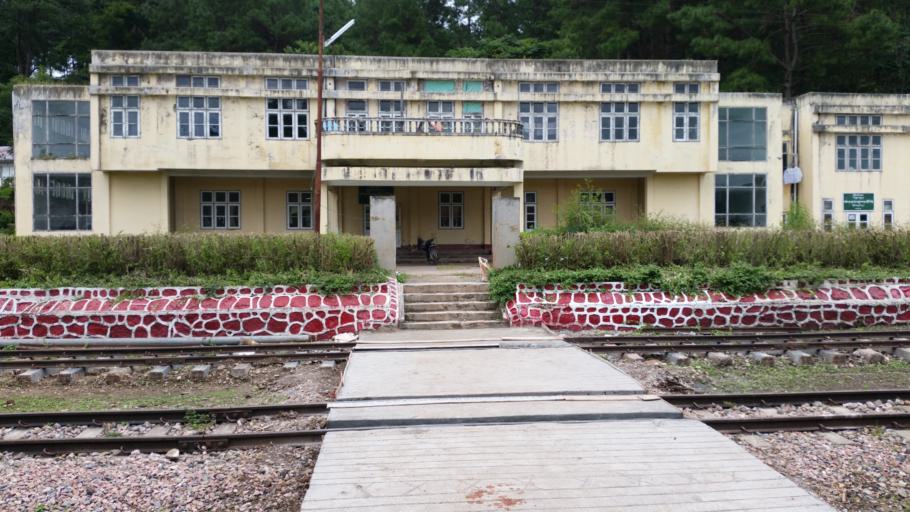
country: MM
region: Mandalay
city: Yamethin
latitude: 20.6290
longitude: 96.5689
